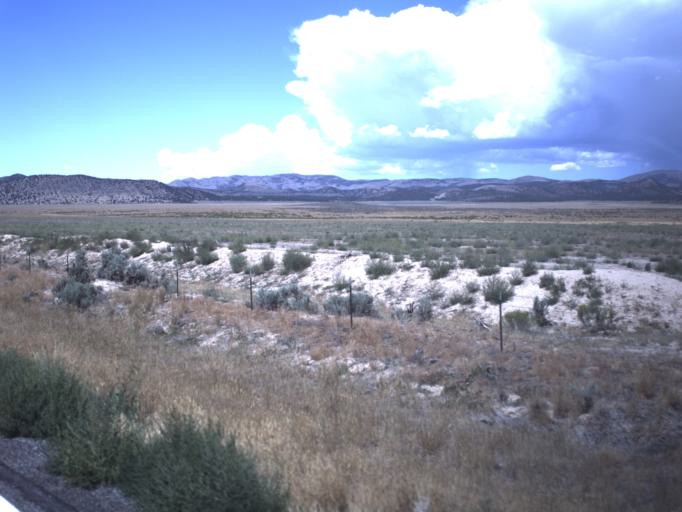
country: US
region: Utah
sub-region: Juab County
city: Nephi
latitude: 39.6974
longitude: -111.9698
